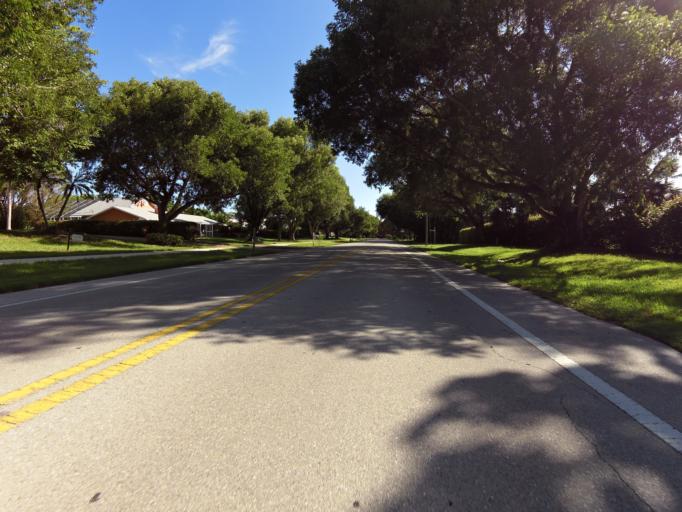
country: US
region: Florida
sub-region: Collier County
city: Naples
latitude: 26.1668
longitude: -81.8059
